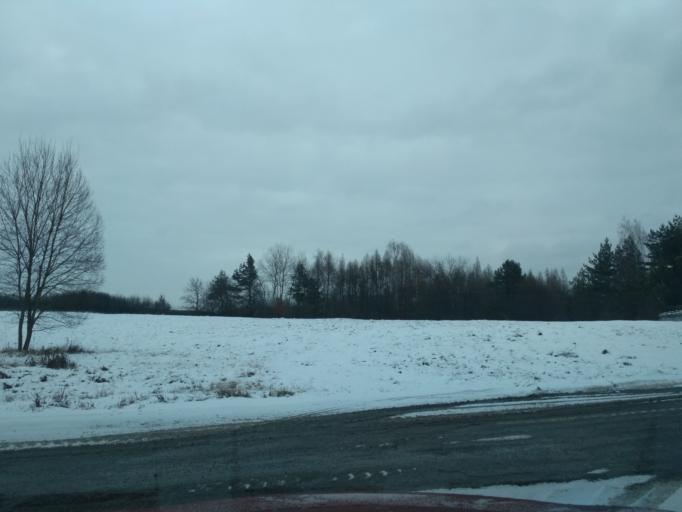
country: SK
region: Presovsky
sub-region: Okres Presov
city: Presov
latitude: 48.9936
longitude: 21.1842
